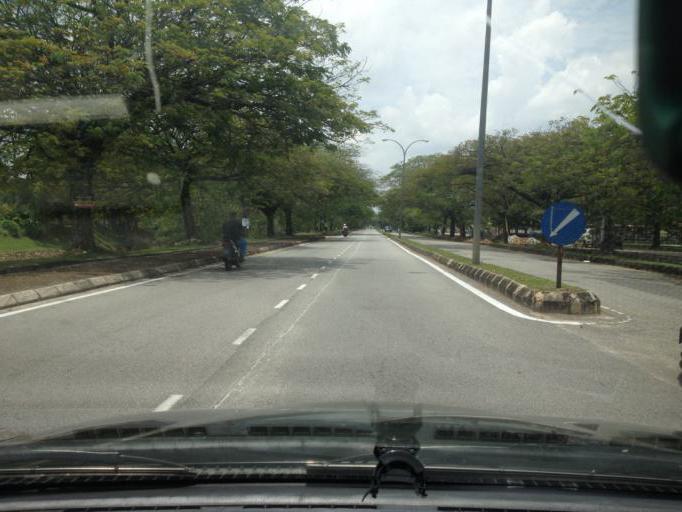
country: MY
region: Kedah
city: Sungai Petani
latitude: 5.6059
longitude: 100.5398
